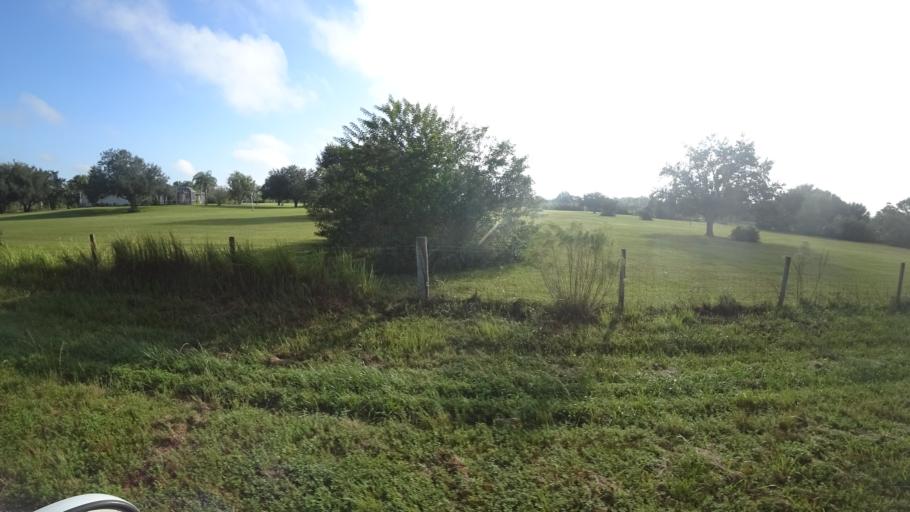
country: US
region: Florida
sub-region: Sarasota County
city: The Meadows
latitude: 27.4152
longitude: -82.3120
